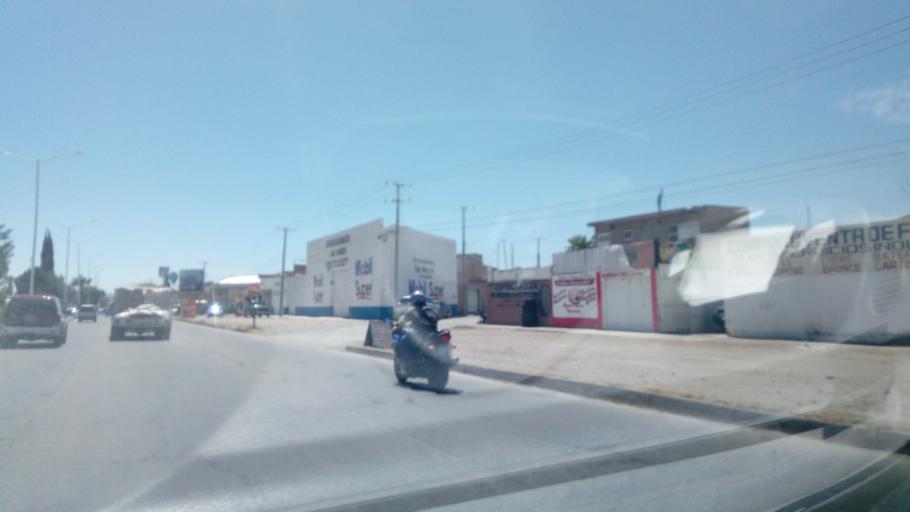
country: MX
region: Durango
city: Victoria de Durango
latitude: 24.0327
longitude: -104.6178
